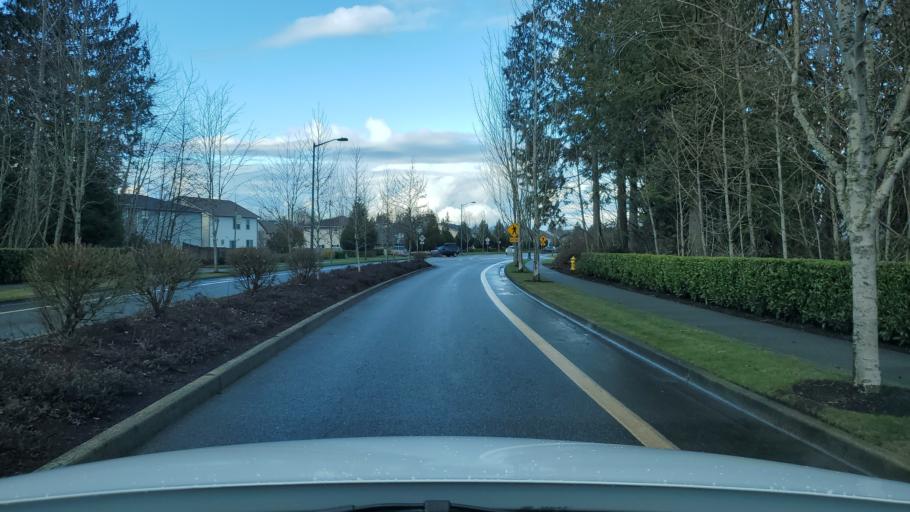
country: US
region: Washington
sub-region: Skagit County
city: Big Lake
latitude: 48.4258
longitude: -122.2785
